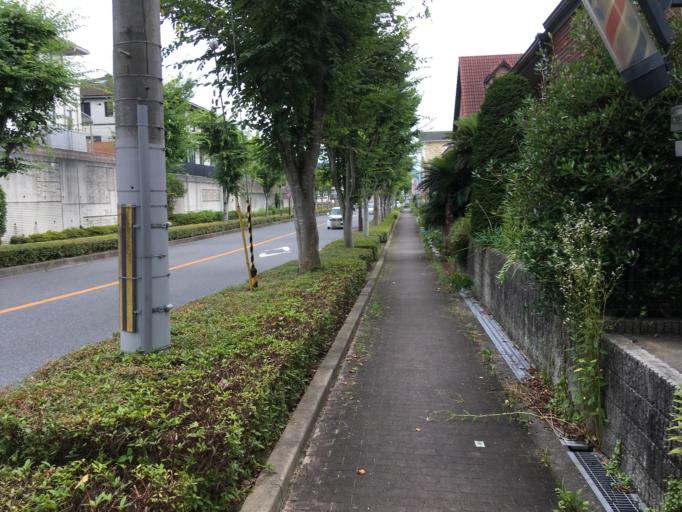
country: JP
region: Nara
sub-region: Ikoma-shi
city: Ikoma
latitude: 34.6759
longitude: 135.7188
